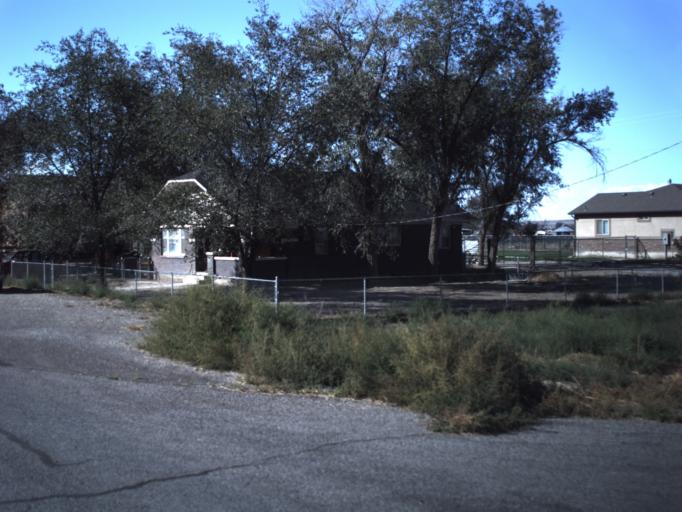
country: US
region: Utah
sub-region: Millard County
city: Delta
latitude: 39.2868
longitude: -112.6528
